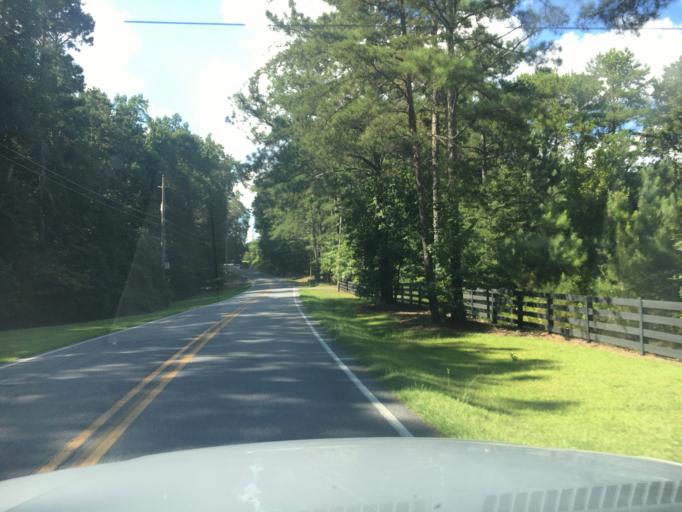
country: US
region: Georgia
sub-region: Cherokee County
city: Holly Springs
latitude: 34.1445
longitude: -84.4634
